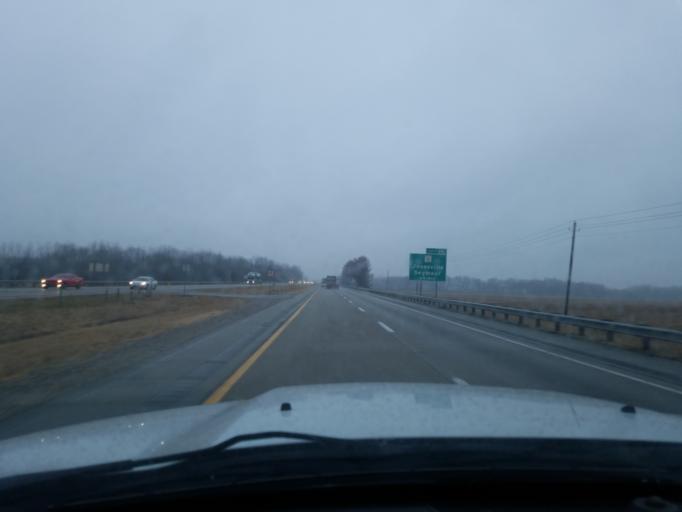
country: US
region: Indiana
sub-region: Jackson County
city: Seymour
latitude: 39.0172
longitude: -85.8780
